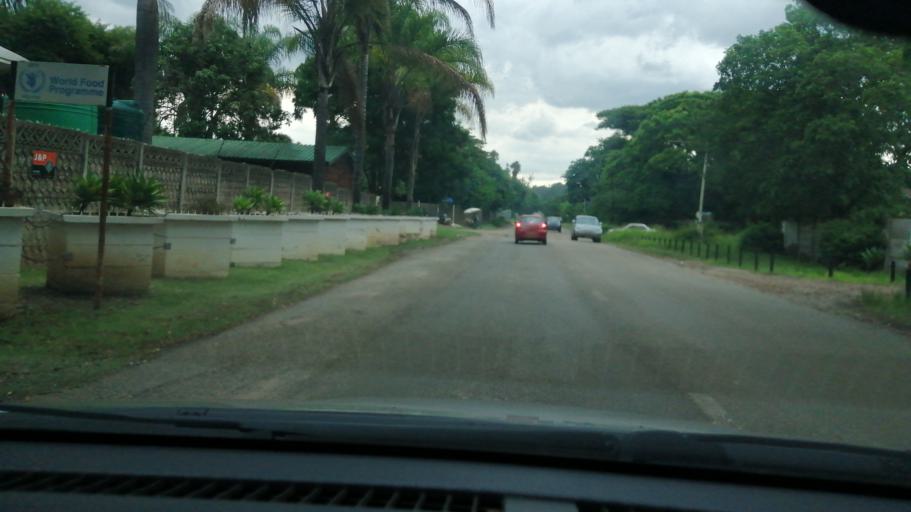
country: ZW
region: Harare
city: Harare
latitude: -17.7993
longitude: 31.0432
